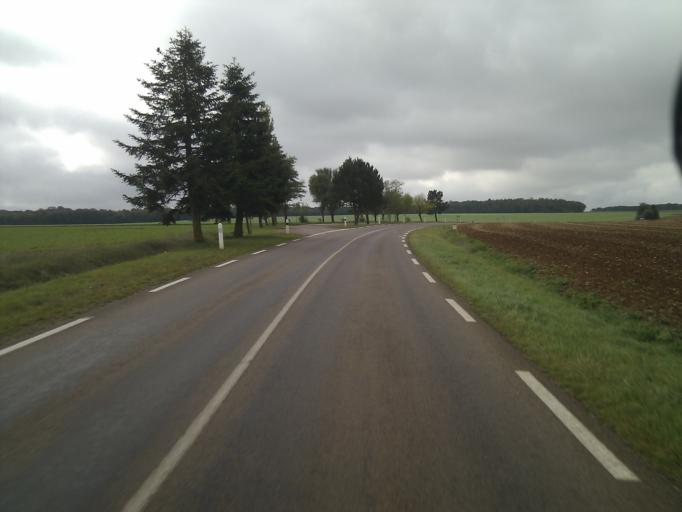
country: FR
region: Champagne-Ardenne
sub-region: Departement de la Haute-Marne
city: Doulaincourt-Saucourt
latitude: 48.2315
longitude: 5.2907
